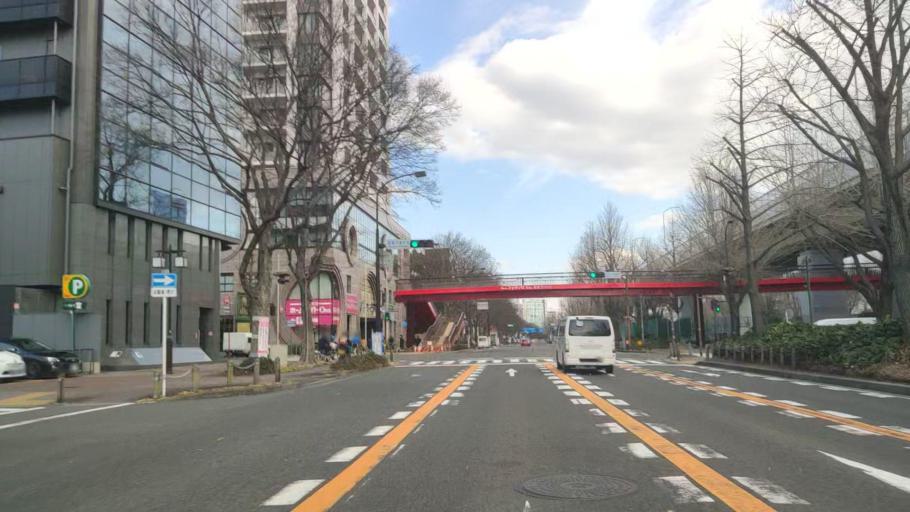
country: JP
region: Aichi
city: Nagoya-shi
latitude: 35.1627
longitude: 136.9015
